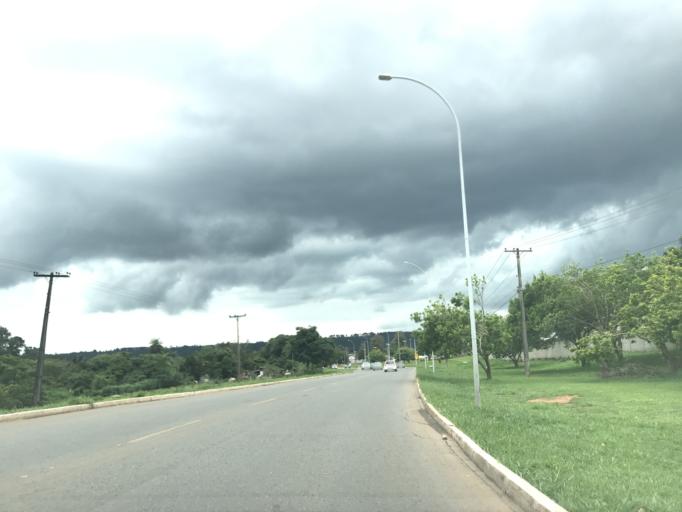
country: BR
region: Federal District
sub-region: Brasilia
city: Brasilia
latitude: -15.6487
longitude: -47.8129
